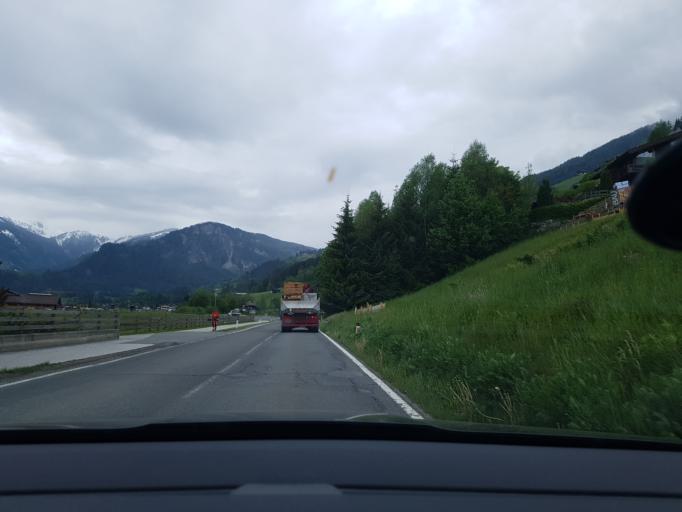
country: AT
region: Salzburg
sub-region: Politischer Bezirk Zell am See
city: Wald im Pinzgau
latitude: 47.2470
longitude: 12.2213
